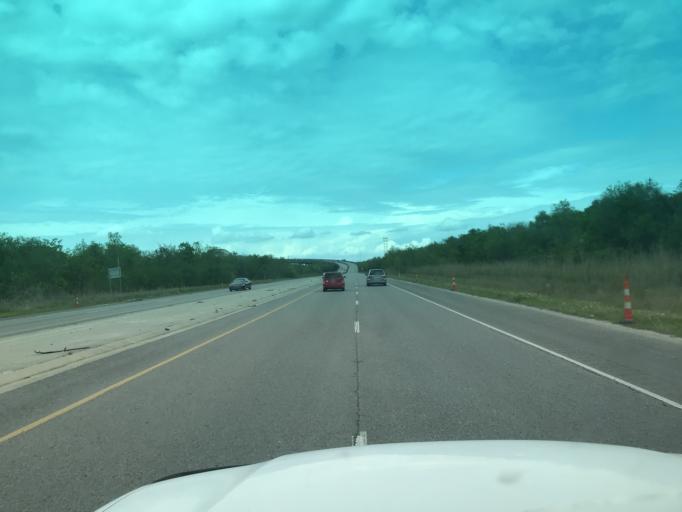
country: US
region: Louisiana
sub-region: Saint Bernard Parish
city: Chalmette
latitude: 29.9927
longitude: -89.9418
